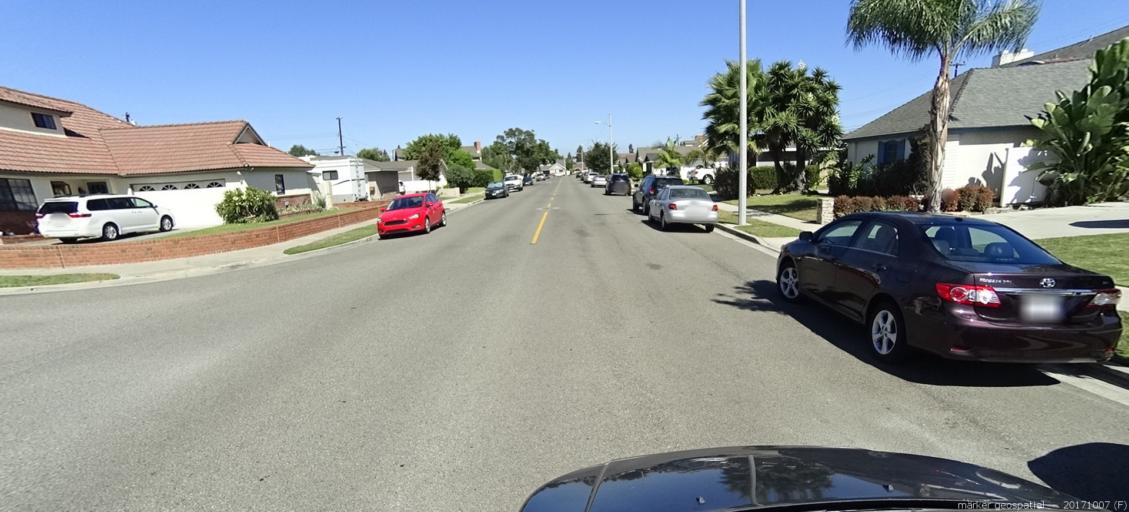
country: US
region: California
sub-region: Orange County
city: Westminster
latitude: 33.7797
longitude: -118.0356
